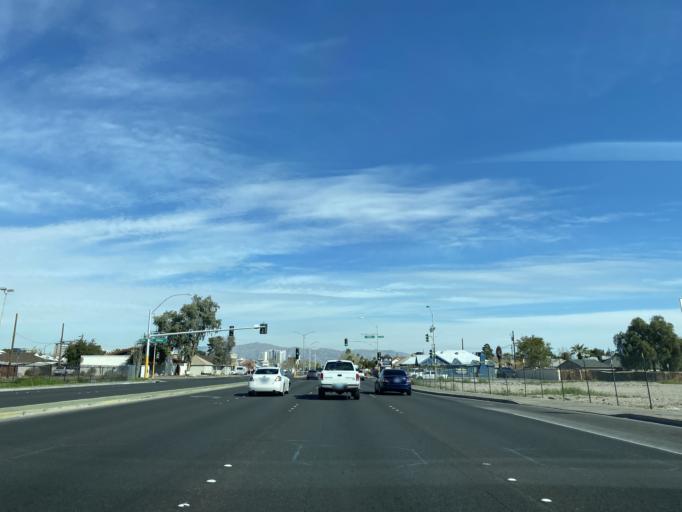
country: US
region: Nevada
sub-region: Clark County
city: Las Vegas
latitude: 36.1507
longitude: -115.1369
